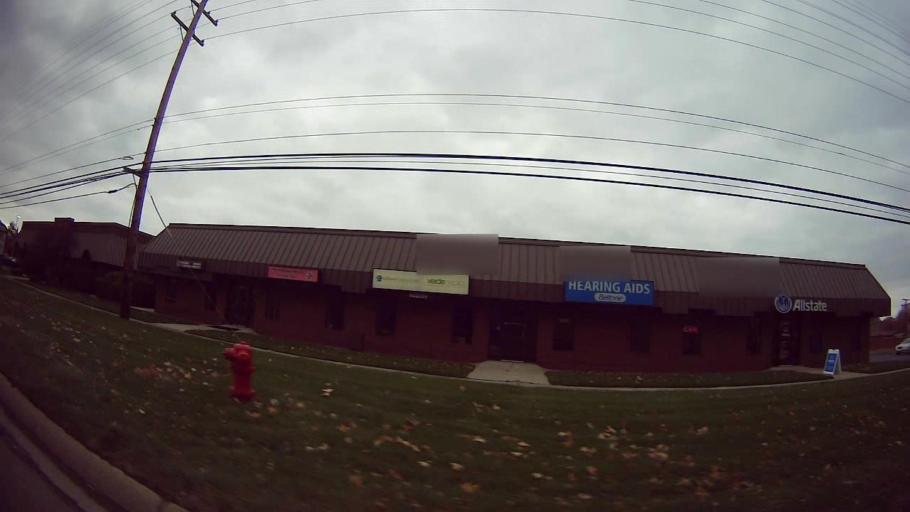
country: US
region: Michigan
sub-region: Macomb County
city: Center Line
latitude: 42.5109
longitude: -83.0071
